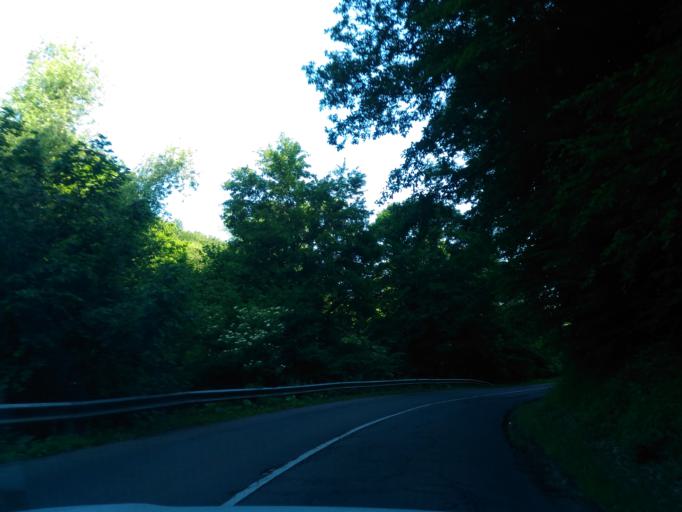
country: HU
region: Baranya
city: Komlo
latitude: 46.1962
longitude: 18.3054
